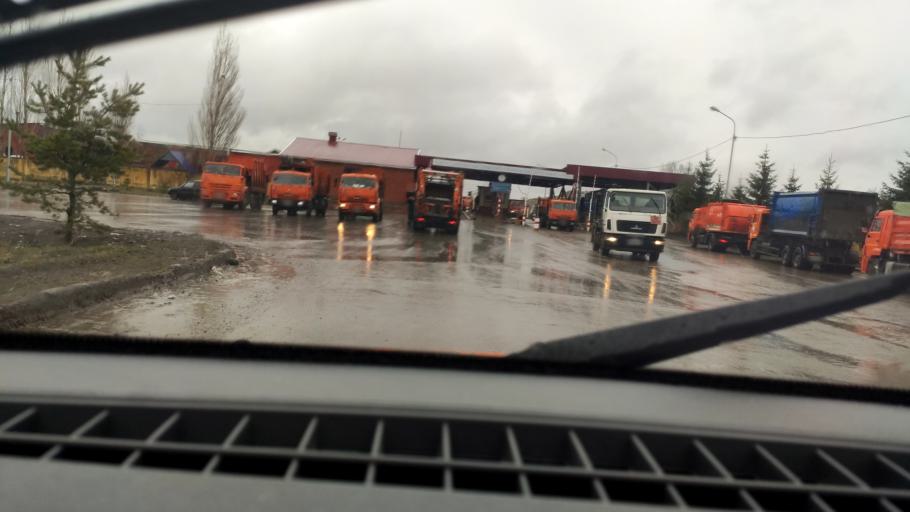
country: RU
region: Bashkortostan
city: Ufa
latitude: 54.8722
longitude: 56.1339
